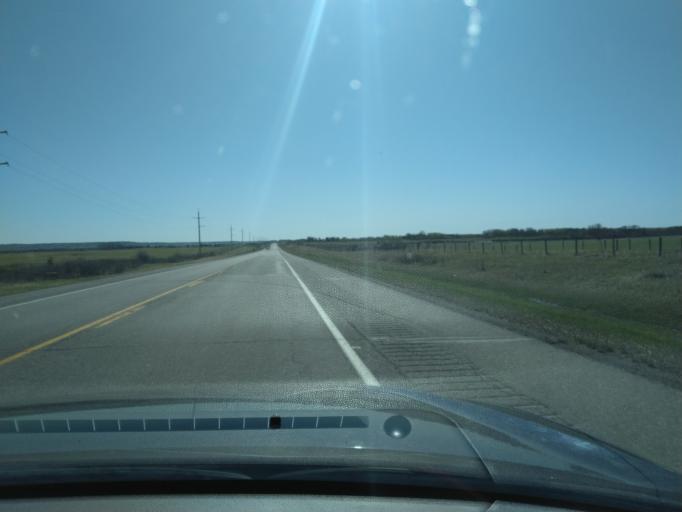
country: CA
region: Alberta
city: Cochrane
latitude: 51.0233
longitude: -114.4151
